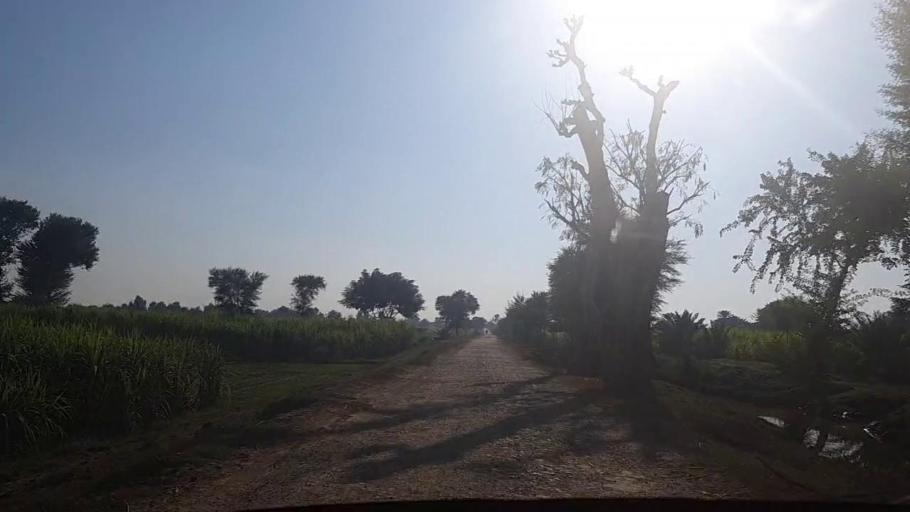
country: PK
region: Sindh
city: Gambat
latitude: 27.3717
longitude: 68.4641
